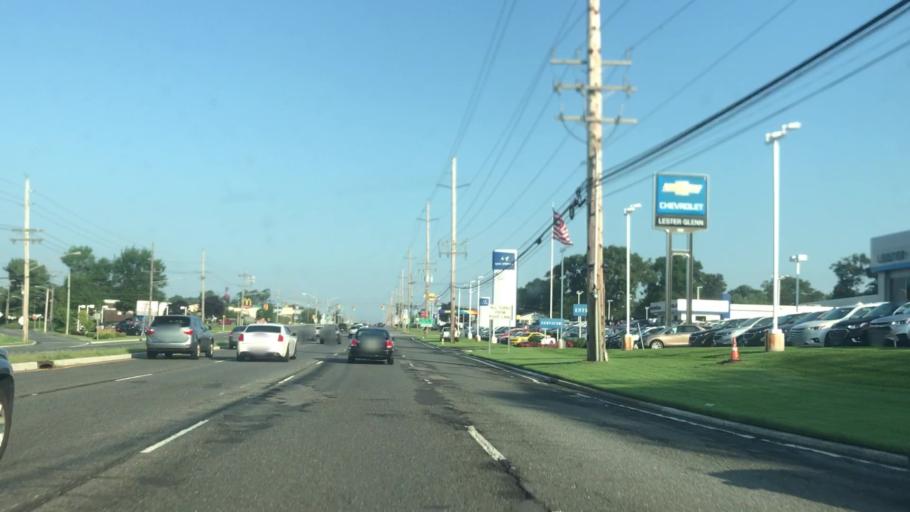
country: US
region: New Jersey
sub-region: Ocean County
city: Pine Beach
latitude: 39.9567
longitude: -74.1681
